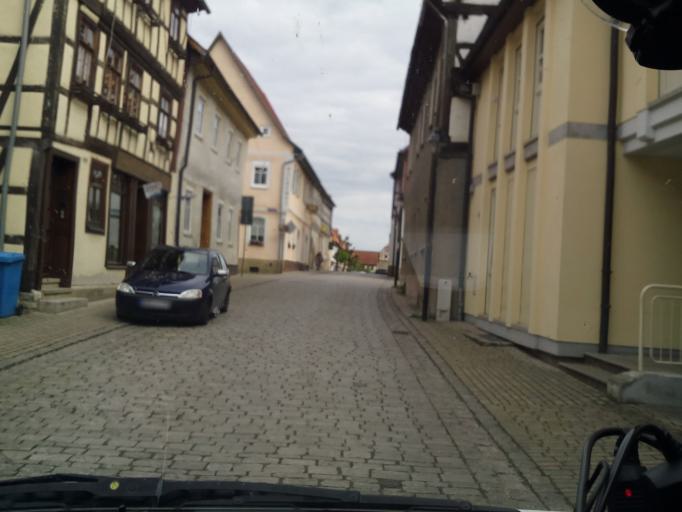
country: DE
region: Thuringia
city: Hellingen
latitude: 50.2808
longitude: 10.7250
